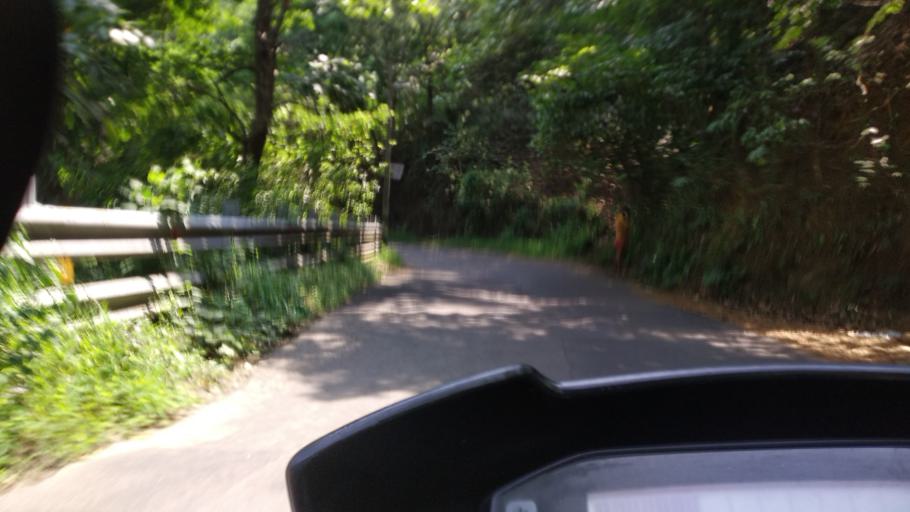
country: IN
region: Kerala
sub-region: Kottayam
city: Erattupetta
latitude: 9.6976
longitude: 76.8641
